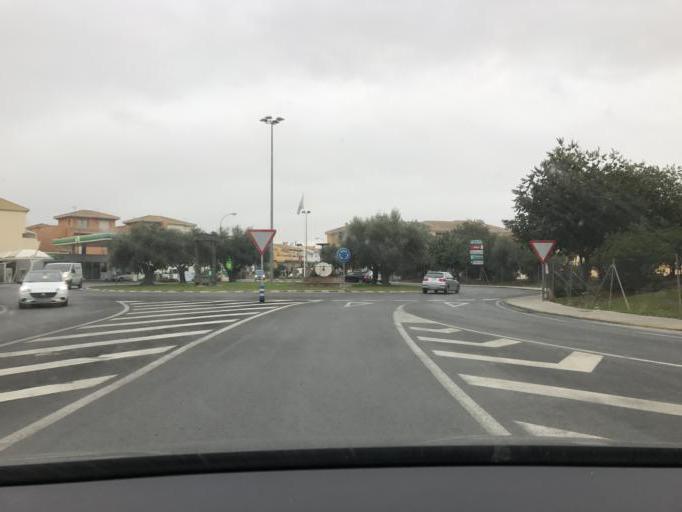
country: ES
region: Andalusia
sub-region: Provincia de Granada
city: Chauchina
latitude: 37.1921
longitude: -3.7240
